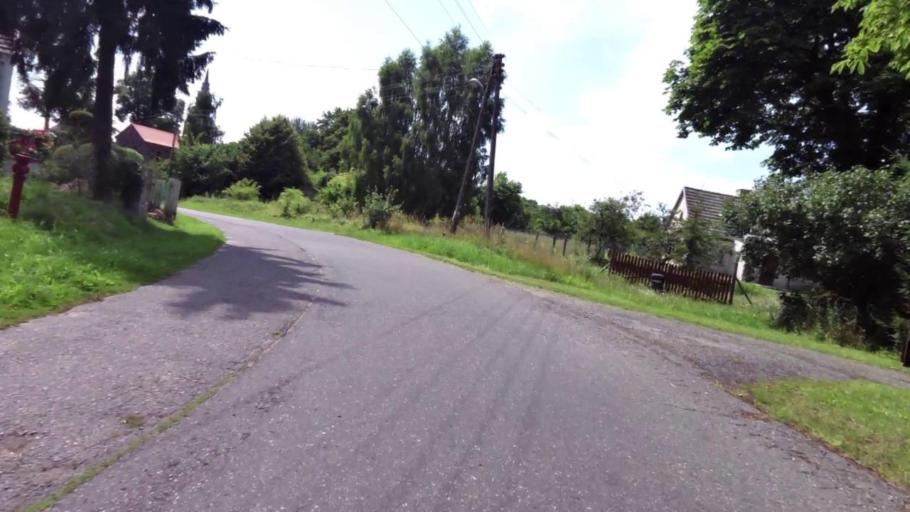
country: PL
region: West Pomeranian Voivodeship
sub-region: Powiat stargardzki
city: Dobrzany
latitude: 53.3763
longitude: 15.3697
